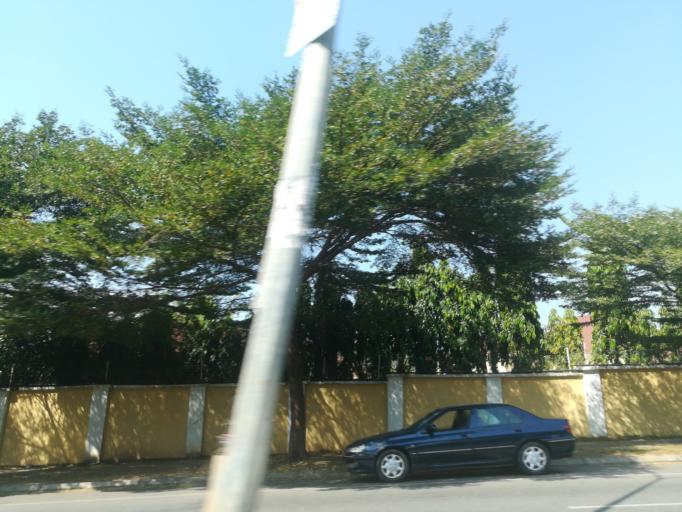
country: NG
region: Abuja Federal Capital Territory
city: Abuja
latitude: 9.0718
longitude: 7.4399
